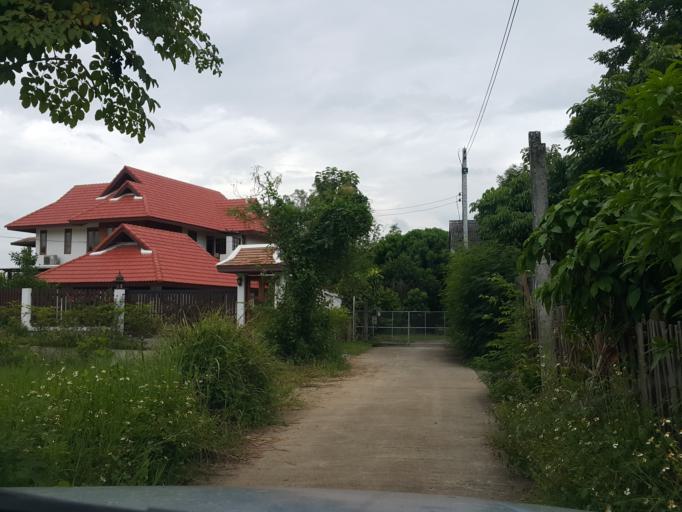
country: TH
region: Chiang Mai
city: San Sai
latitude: 18.8362
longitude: 99.1267
